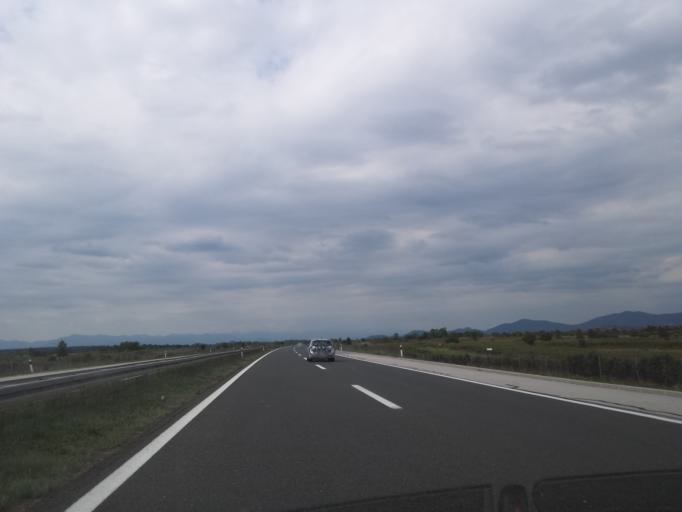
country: HR
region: Licko-Senjska
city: Gospic
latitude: 44.4822
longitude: 15.5562
